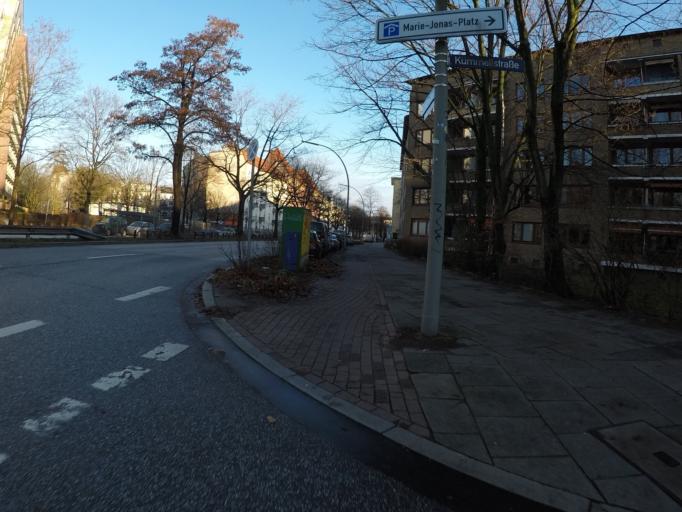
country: DE
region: Hamburg
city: Hamburg-Nord
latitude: 53.5905
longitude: 9.9843
